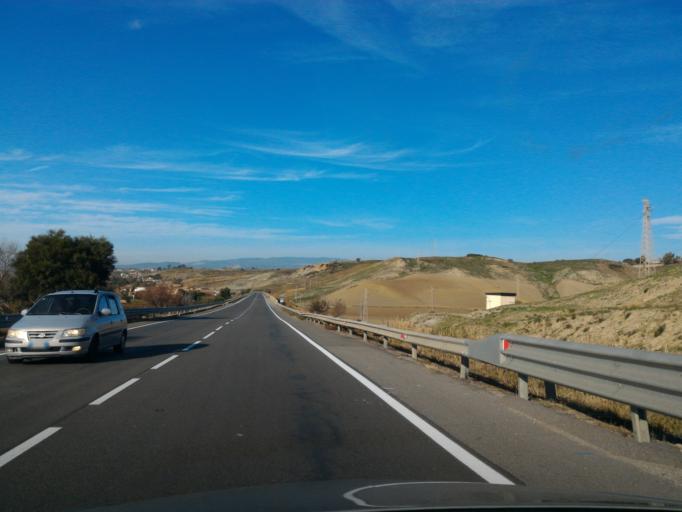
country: IT
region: Calabria
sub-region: Provincia di Crotone
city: Le Castella
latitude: 38.9384
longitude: 16.9891
